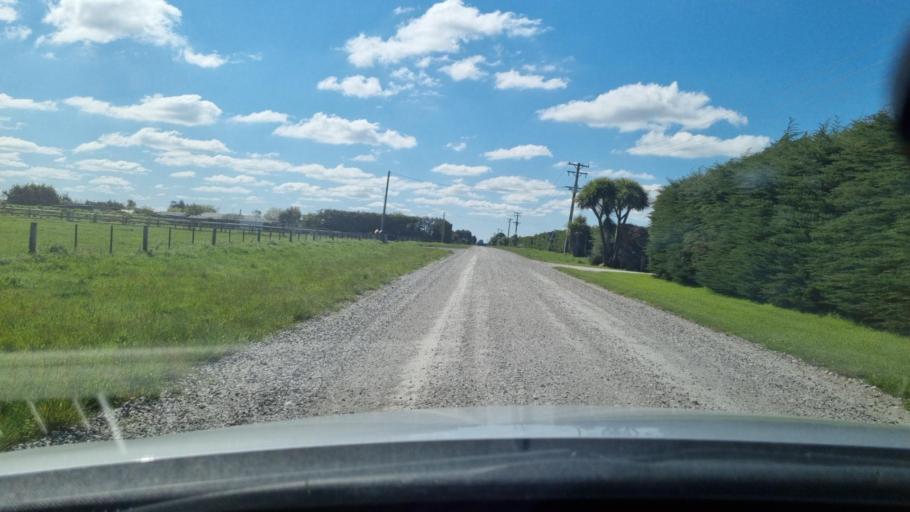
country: NZ
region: Southland
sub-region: Invercargill City
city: Invercargill
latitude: -46.3774
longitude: 168.2983
